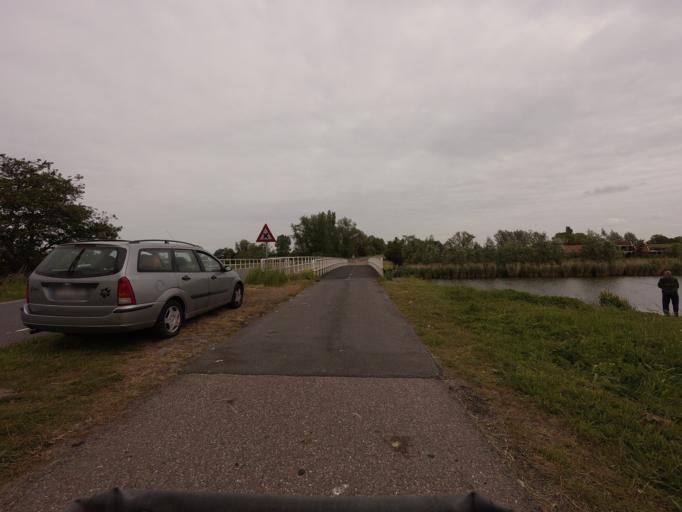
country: NL
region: North Holland
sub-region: Gemeente Medemblik
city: Medemblik
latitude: 52.7550
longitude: 5.1188
